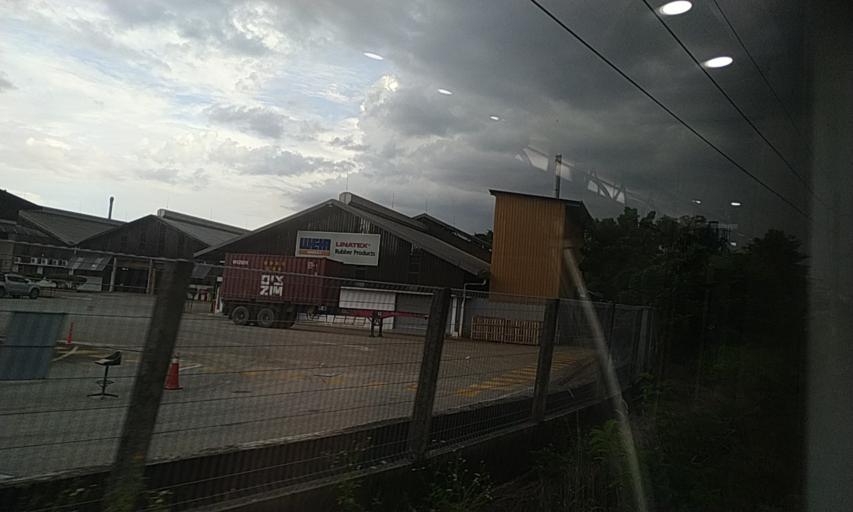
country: MY
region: Kuala Lumpur
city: Kuala Lumpur
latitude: 3.2293
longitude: 101.6734
